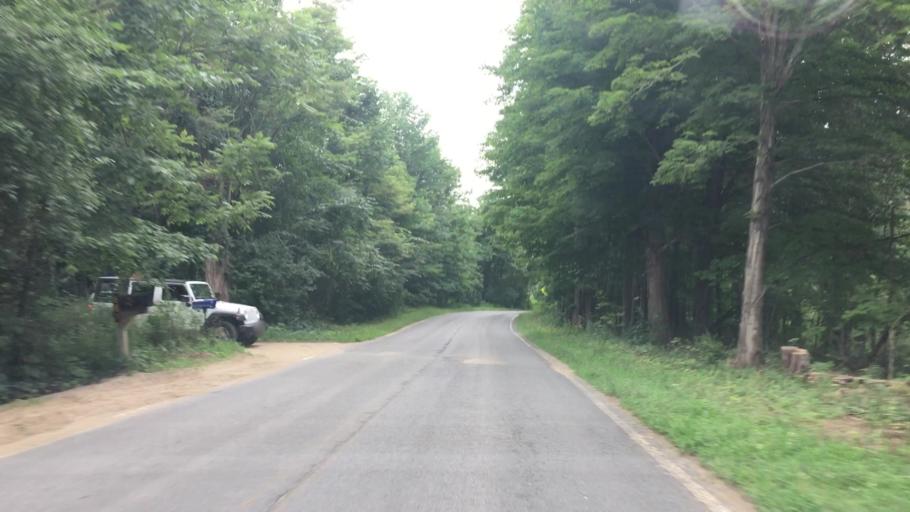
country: US
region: New York
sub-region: Essex County
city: Keeseville
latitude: 44.4383
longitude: -73.6167
